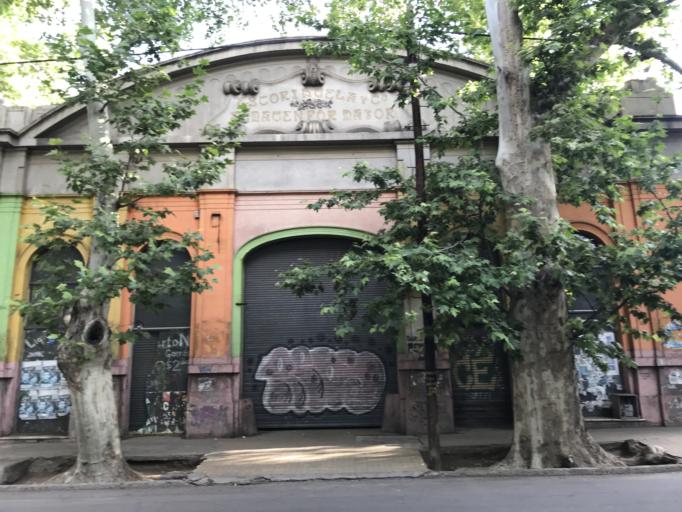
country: AR
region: Mendoza
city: Mendoza
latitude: -32.8837
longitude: -68.8356
